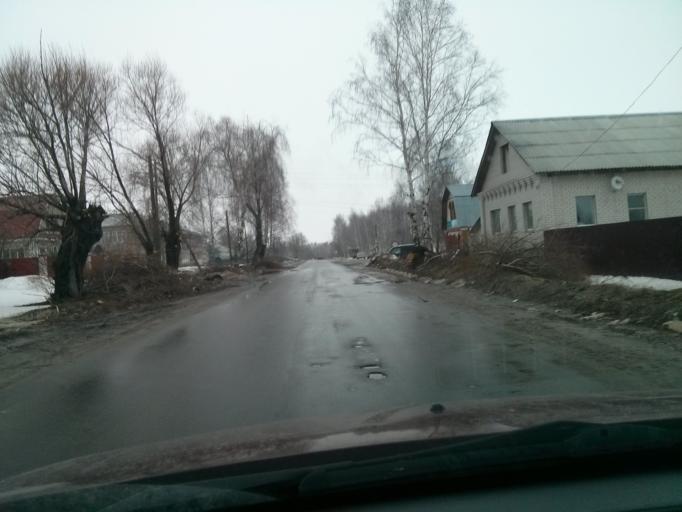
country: RU
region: Nizjnij Novgorod
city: Shimorskoye
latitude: 55.3417
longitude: 41.9290
